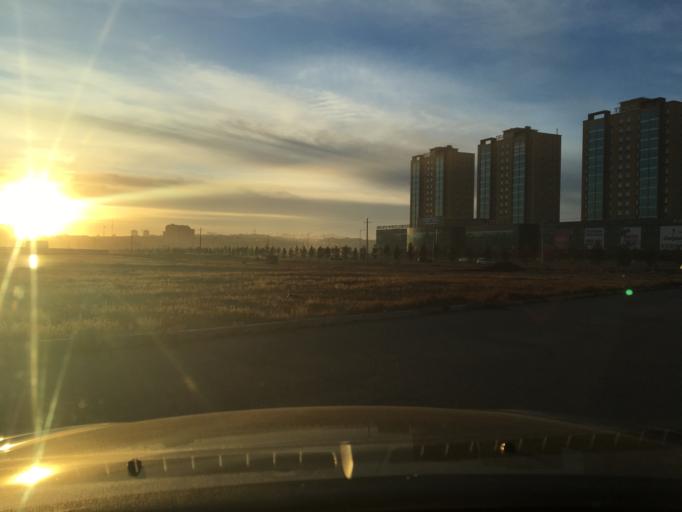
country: MN
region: Ulaanbaatar
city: Ulaanbaatar
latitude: 47.8633
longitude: 106.8083
